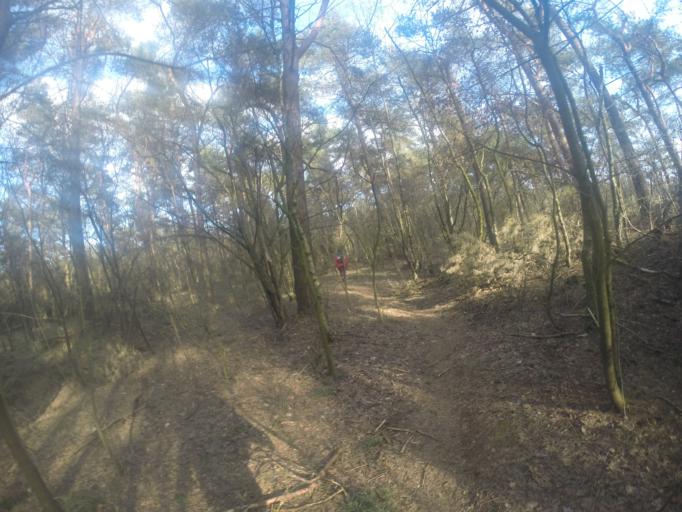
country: NL
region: Gelderland
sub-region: Gemeente Lochem
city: Almen
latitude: 52.1277
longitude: 6.3397
